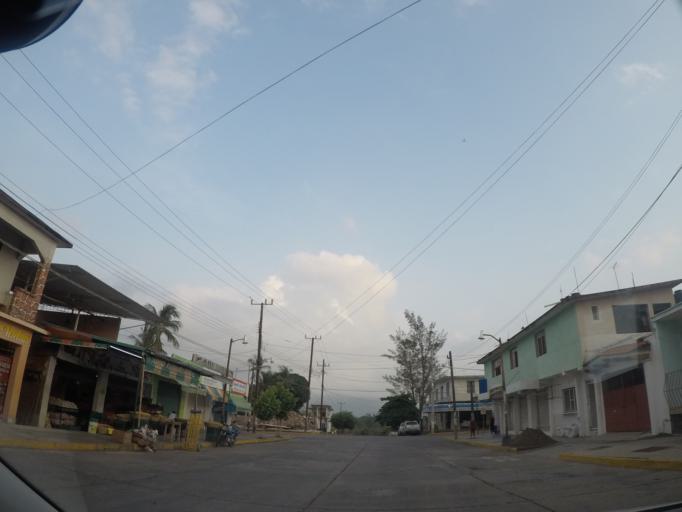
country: MX
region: Oaxaca
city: Matias Romero
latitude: 16.8762
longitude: -95.0420
